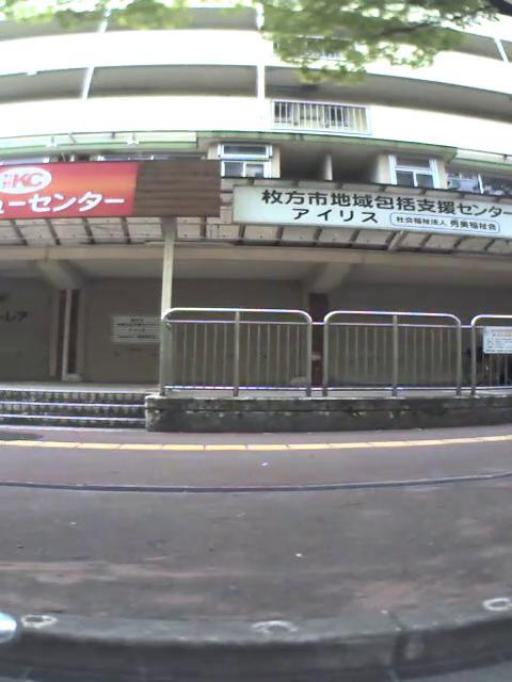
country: JP
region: Osaka
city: Hirakata
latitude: 34.7881
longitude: 135.6468
